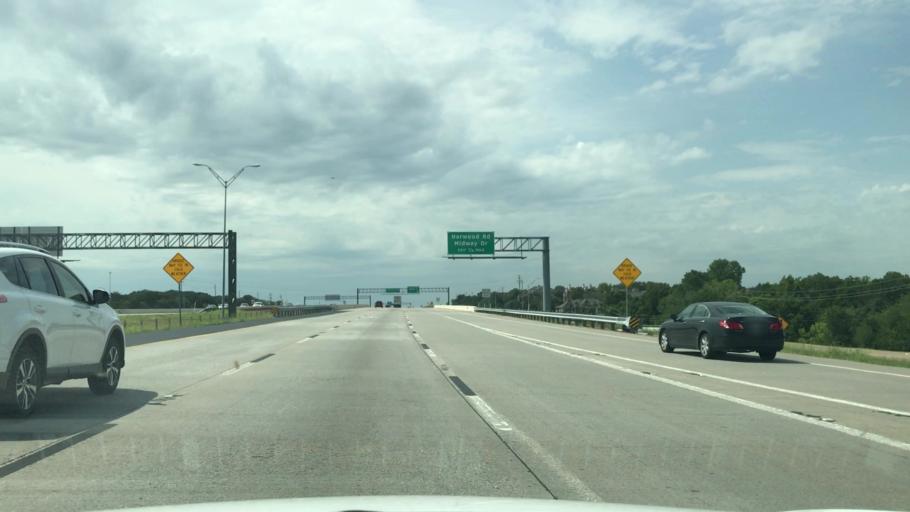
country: US
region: Texas
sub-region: Tarrant County
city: Euless
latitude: 32.8625
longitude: -97.0646
